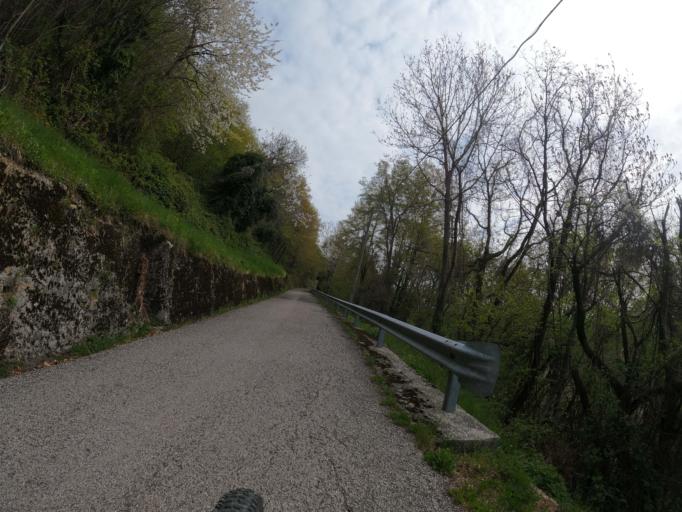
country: IT
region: Friuli Venezia Giulia
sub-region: Provincia di Udine
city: Clodig
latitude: 46.1362
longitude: 13.5969
